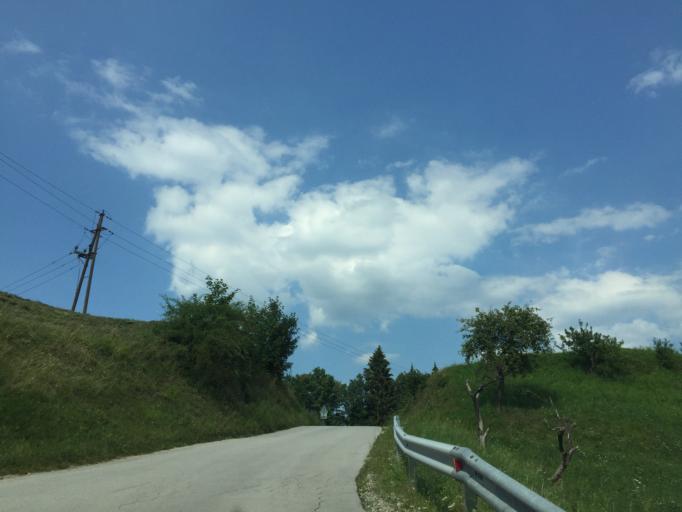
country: SI
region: Sostanj
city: Ravne
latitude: 46.4154
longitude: 15.1090
